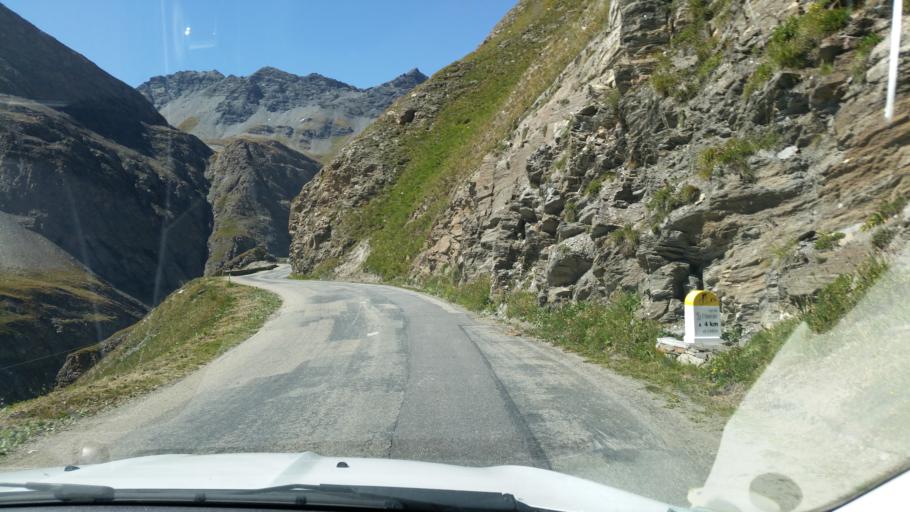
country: FR
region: Rhone-Alpes
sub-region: Departement de la Savoie
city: Val-d'Isere
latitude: 45.4005
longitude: 7.0420
